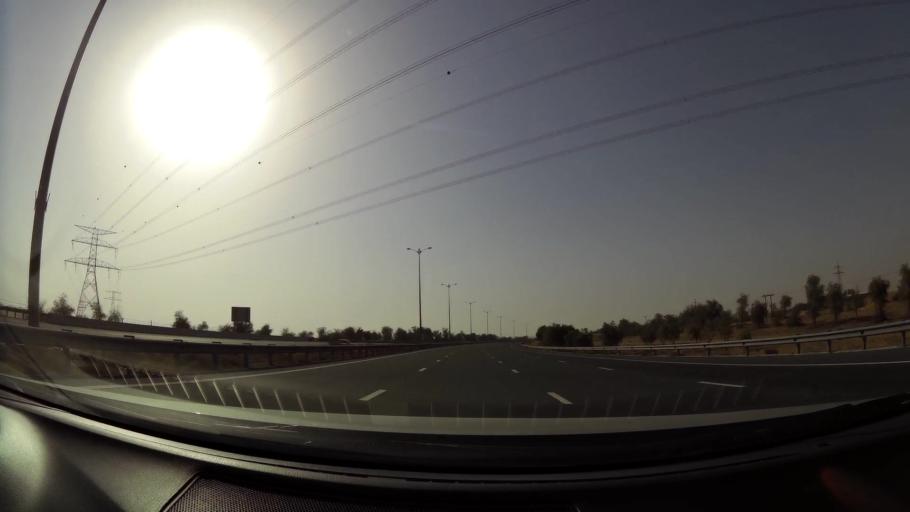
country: OM
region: Al Buraimi
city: Al Buraymi
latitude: 24.6550
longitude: 55.6972
